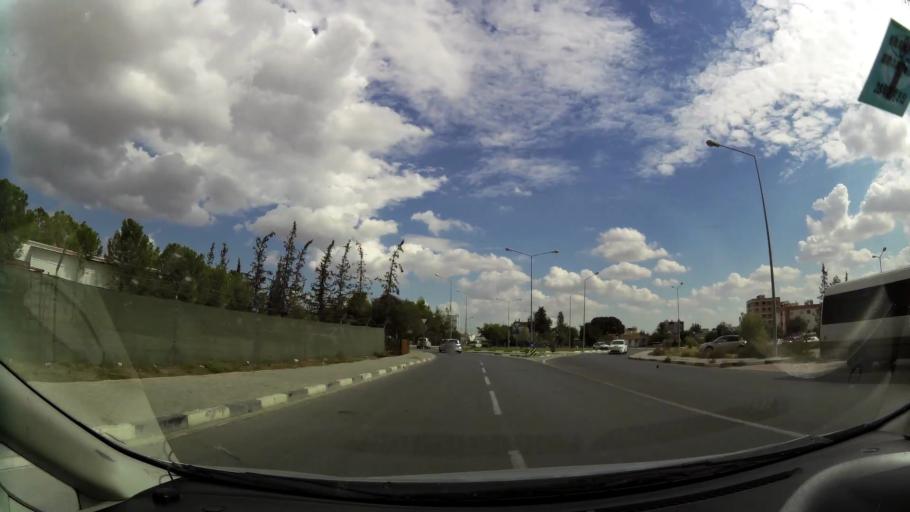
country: CY
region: Lefkosia
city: Nicosia
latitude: 35.1993
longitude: 33.3568
